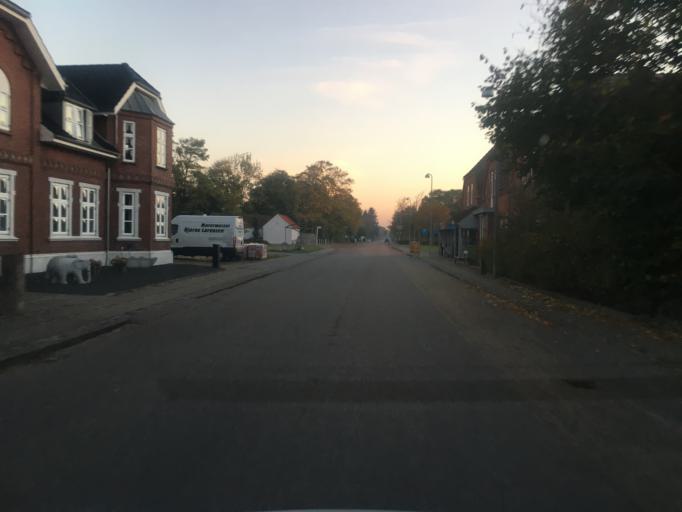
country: DE
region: Schleswig-Holstein
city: Bramstedtlund
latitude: 54.9416
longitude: 9.0860
